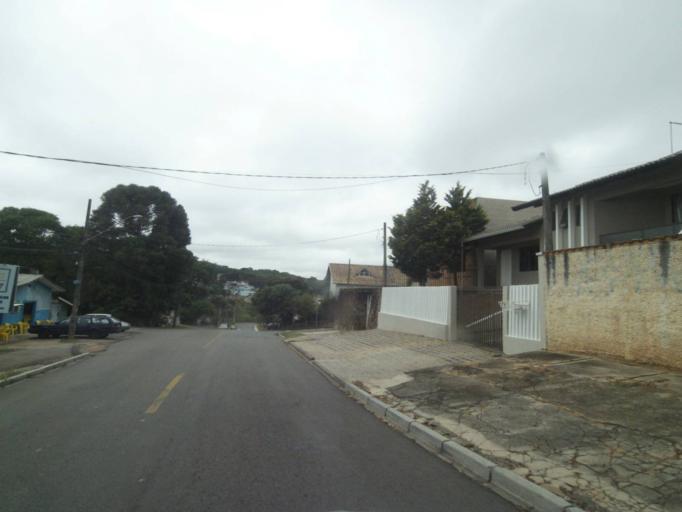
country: BR
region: Parana
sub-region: Curitiba
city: Curitiba
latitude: -25.4257
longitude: -49.3407
